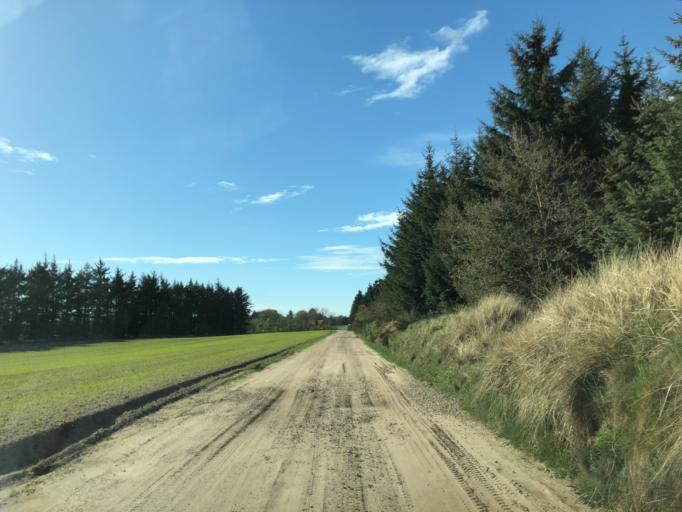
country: DK
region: Central Jutland
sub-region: Holstebro Kommune
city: Ulfborg
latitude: 56.2488
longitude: 8.3334
